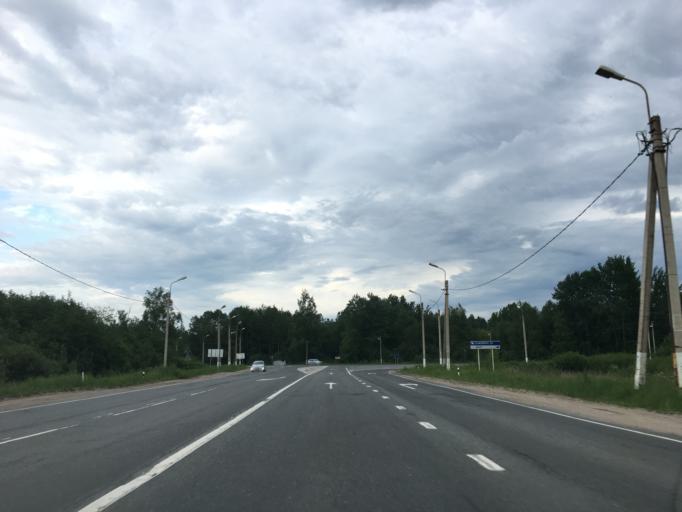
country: RU
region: Pskov
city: Pskov
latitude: 57.8304
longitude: 28.4317
